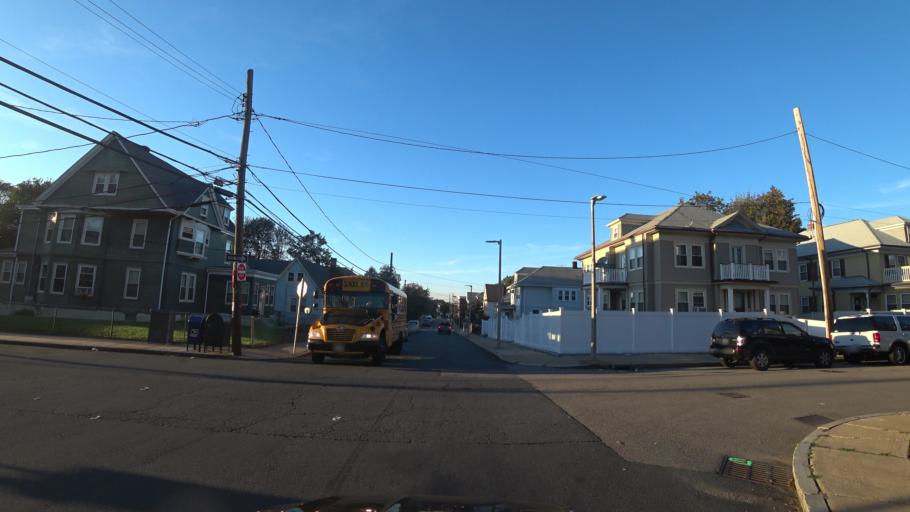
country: US
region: Massachusetts
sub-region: Norfolk County
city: Milton
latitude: 42.2801
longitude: -71.0754
